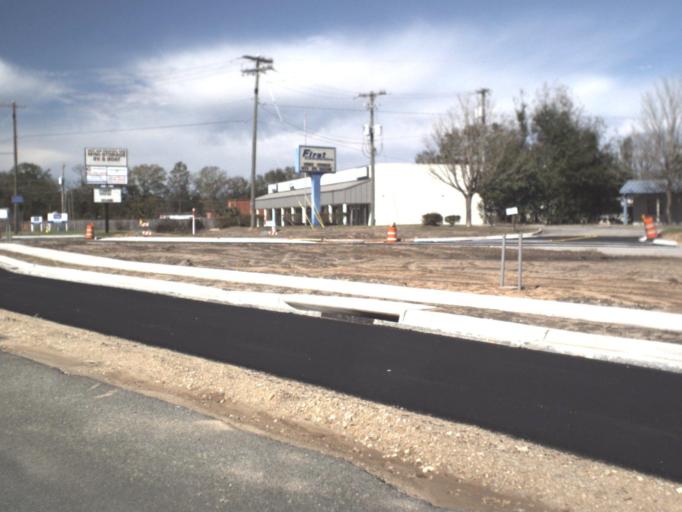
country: US
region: Florida
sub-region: Leon County
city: Tallahassee
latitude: 30.4364
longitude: -84.3505
